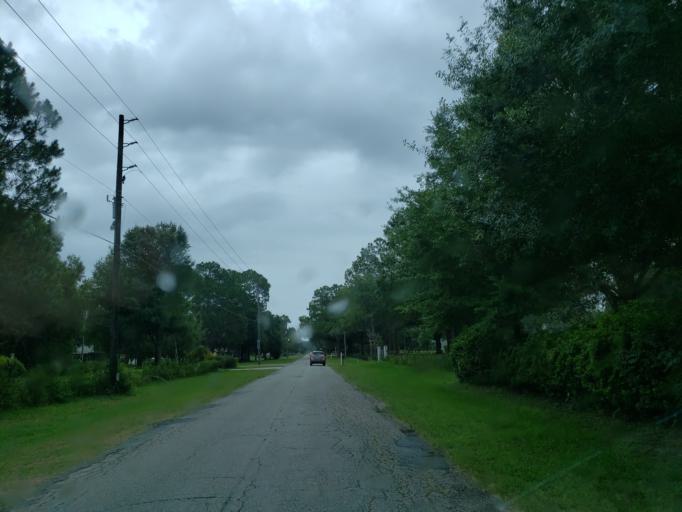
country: US
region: Florida
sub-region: Pasco County
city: Wesley Chapel
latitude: 28.2643
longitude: -82.3477
